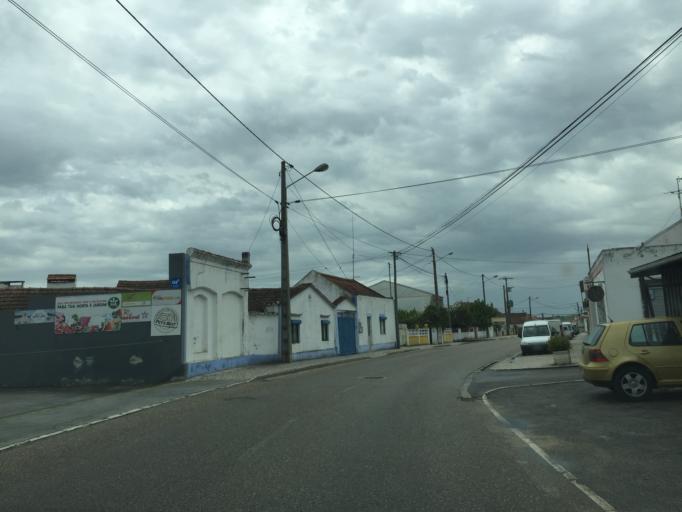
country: PT
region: Lisbon
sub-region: Azambuja
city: Aveiras de Cima
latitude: 39.1418
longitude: -8.9000
